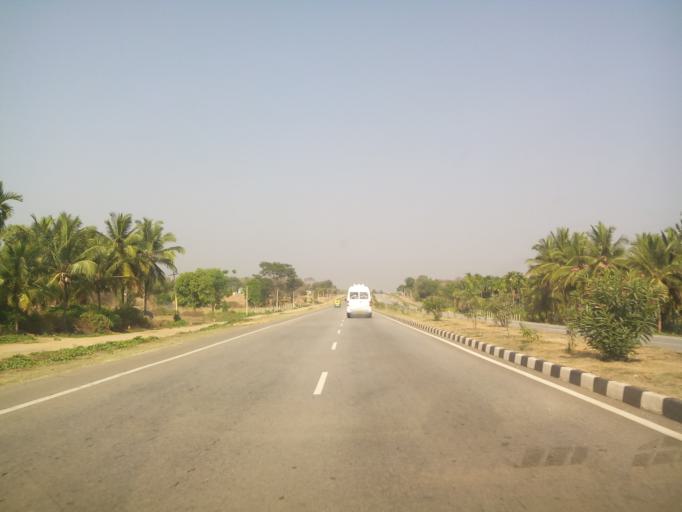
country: IN
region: Karnataka
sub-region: Tumkur
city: Kunigal
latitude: 13.0204
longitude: 77.0628
